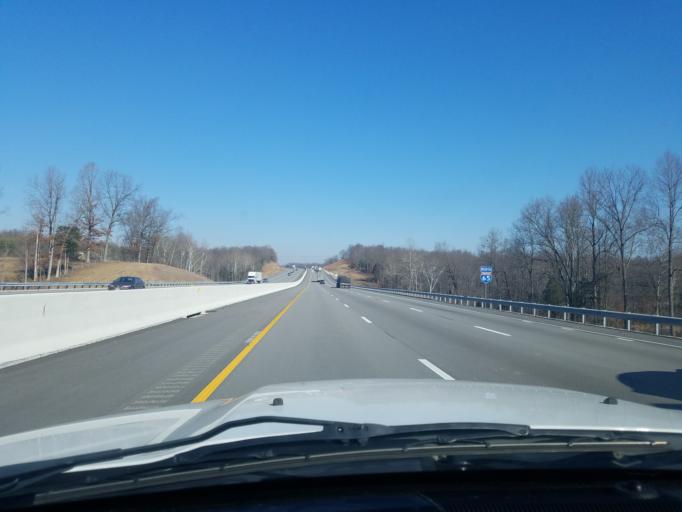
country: US
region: Kentucky
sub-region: Hart County
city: Munfordville
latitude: 37.3877
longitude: -85.8855
